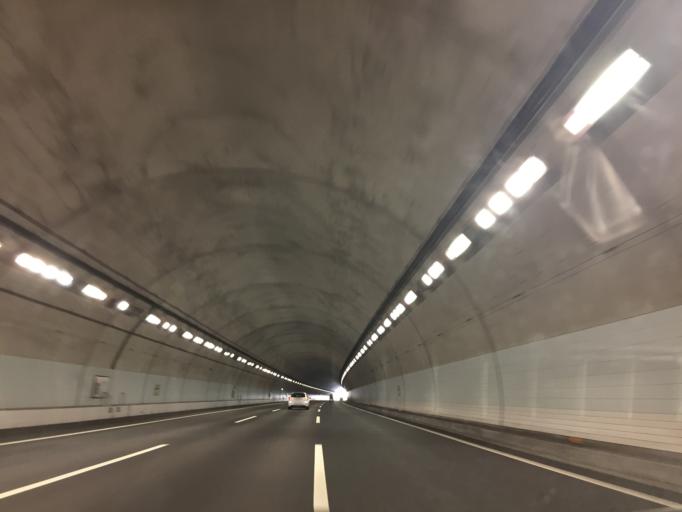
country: JP
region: Shizuoka
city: Kakegawa
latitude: 34.8404
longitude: 138.0281
